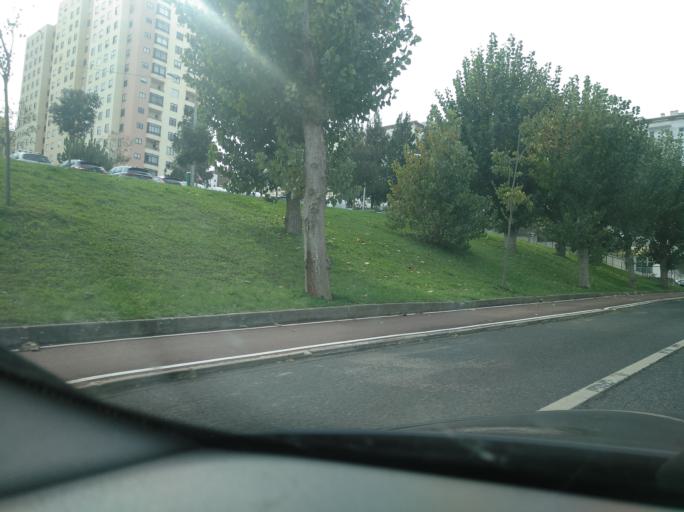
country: PT
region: Lisbon
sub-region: Amadora
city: Amadora
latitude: 38.7396
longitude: -9.2228
